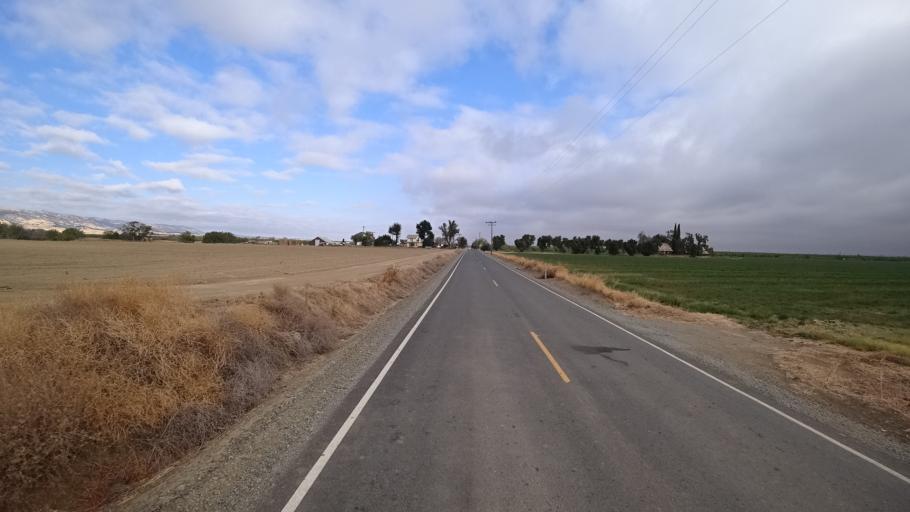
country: US
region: California
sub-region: Yolo County
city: Esparto
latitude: 38.7558
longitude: -122.0443
